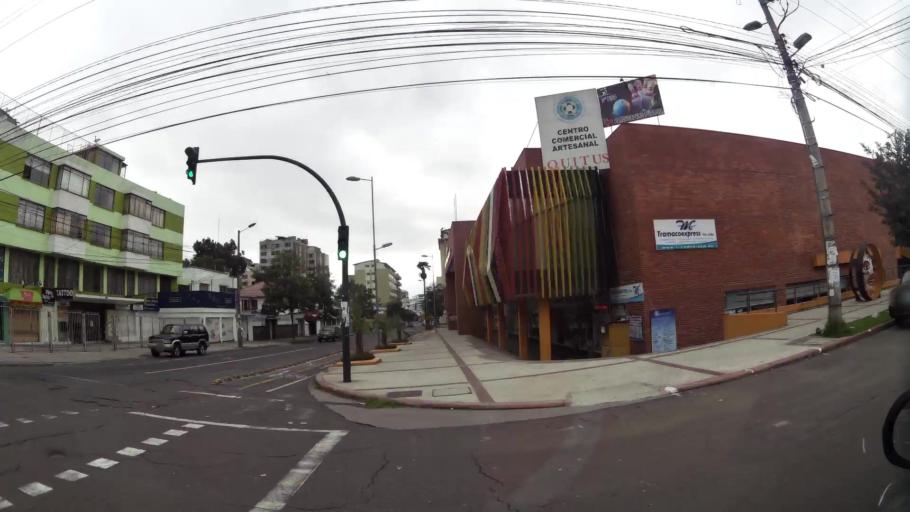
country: EC
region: Pichincha
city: Quito
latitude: -0.2027
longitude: -78.5000
